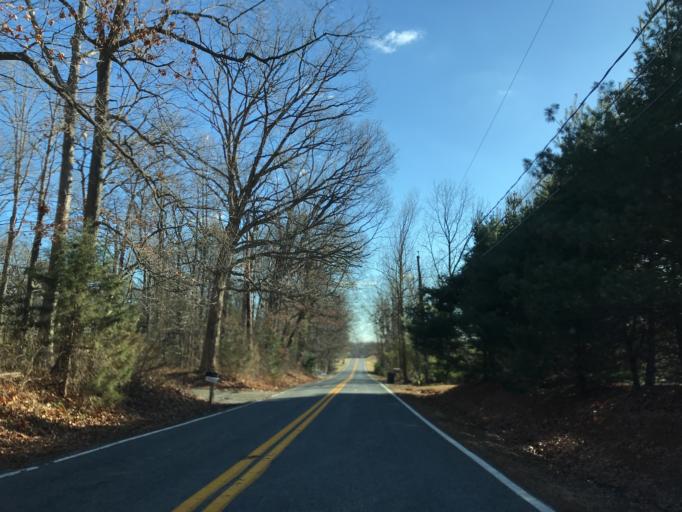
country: US
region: Maryland
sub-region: Howard County
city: Fulton
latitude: 39.1472
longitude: -76.9202
